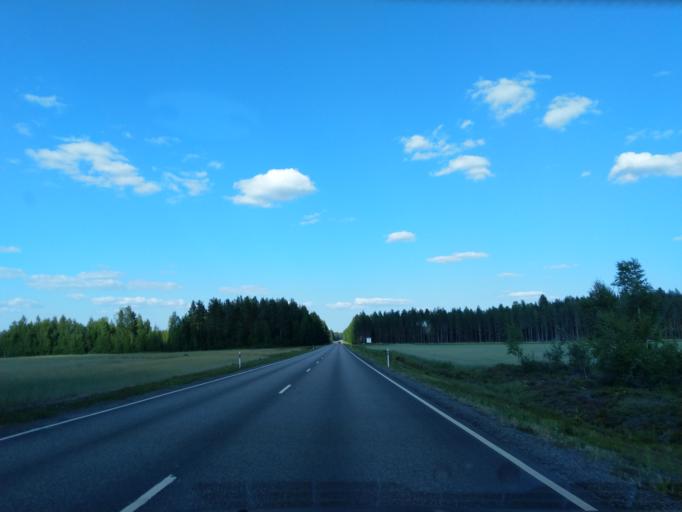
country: FI
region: Pirkanmaa
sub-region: Luoteis-Pirkanmaa
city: Kihnioe
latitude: 62.2097
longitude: 23.2403
